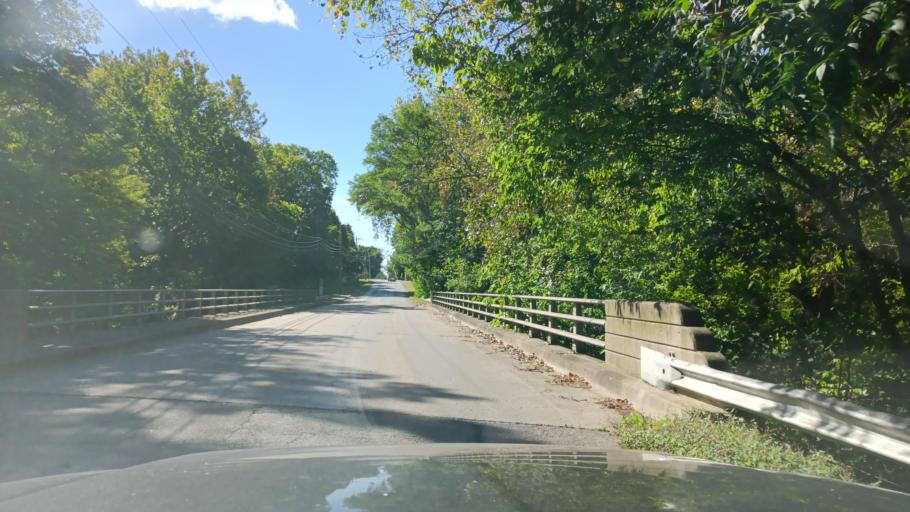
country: US
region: Indiana
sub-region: Fountain County
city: Covington
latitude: 40.1344
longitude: -87.3860
